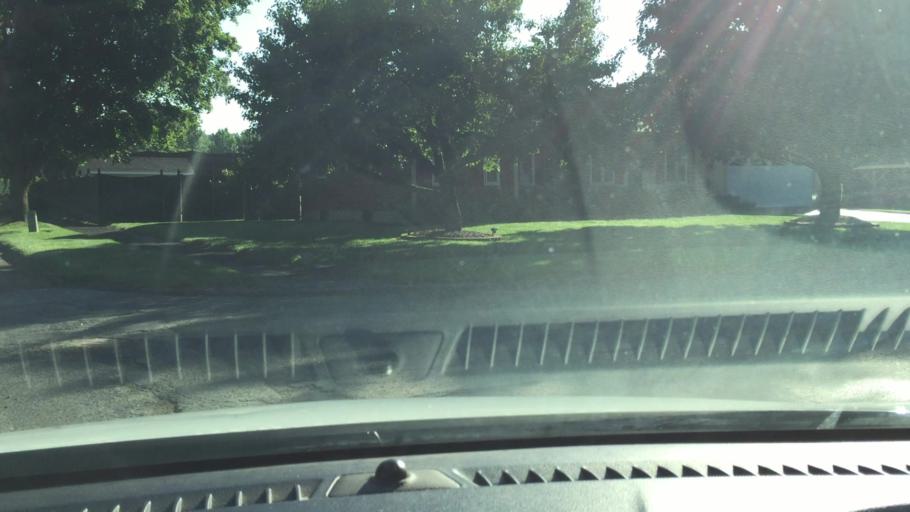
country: US
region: Massachusetts
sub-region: Berkshire County
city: Pittsfield
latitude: 42.4193
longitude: -73.2343
